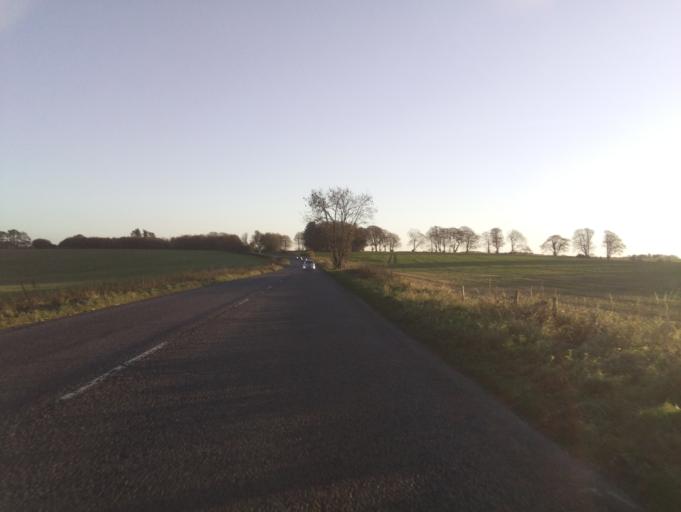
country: GB
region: England
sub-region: Wiltshire
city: Chicklade
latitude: 51.1110
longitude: -2.1691
